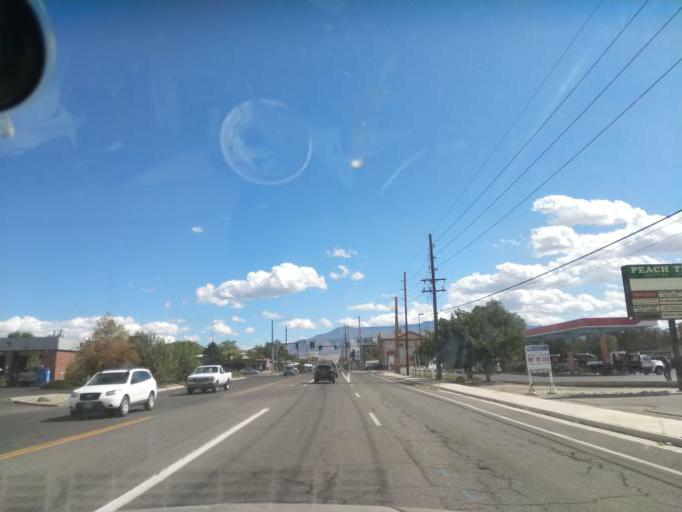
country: US
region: Colorado
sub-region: Mesa County
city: Clifton
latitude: 39.0917
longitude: -108.4518
